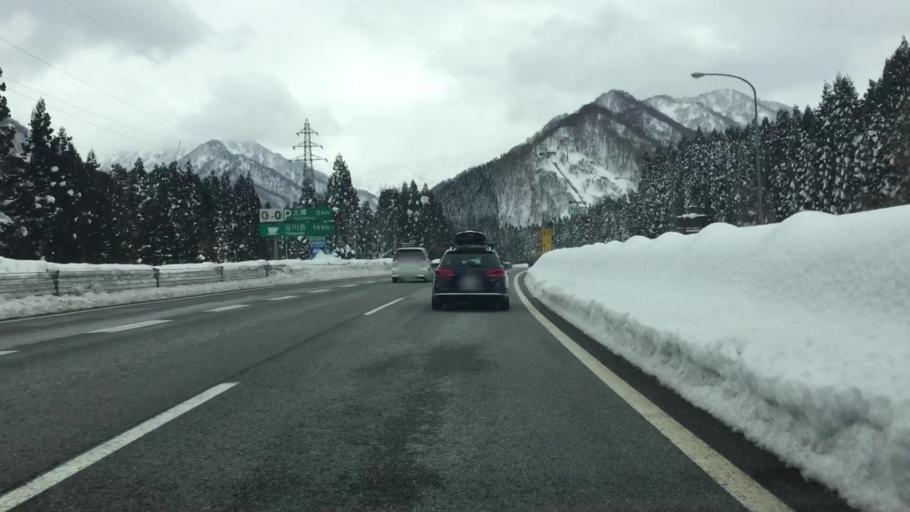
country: JP
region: Niigata
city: Shiozawa
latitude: 36.8848
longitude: 138.8515
